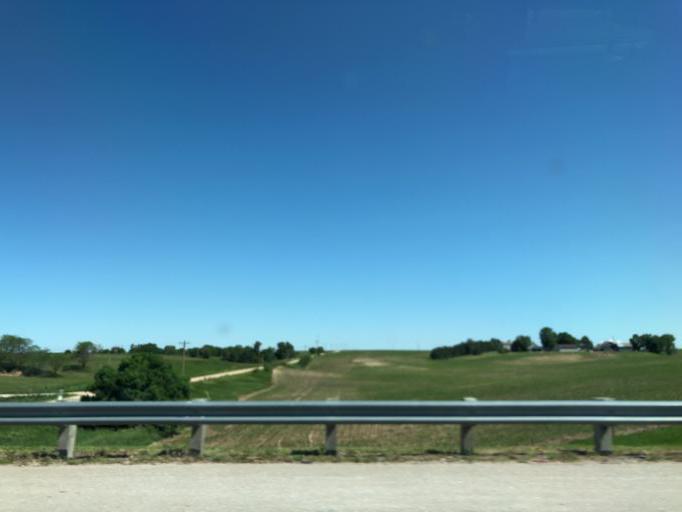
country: US
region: Nebraska
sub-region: York County
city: York
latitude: 40.8213
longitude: -97.4054
